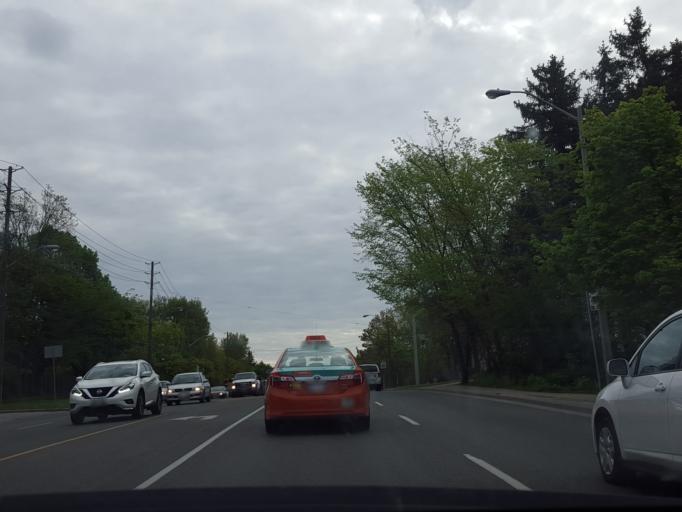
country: CA
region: Ontario
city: Willowdale
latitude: 43.7854
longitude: -79.3906
